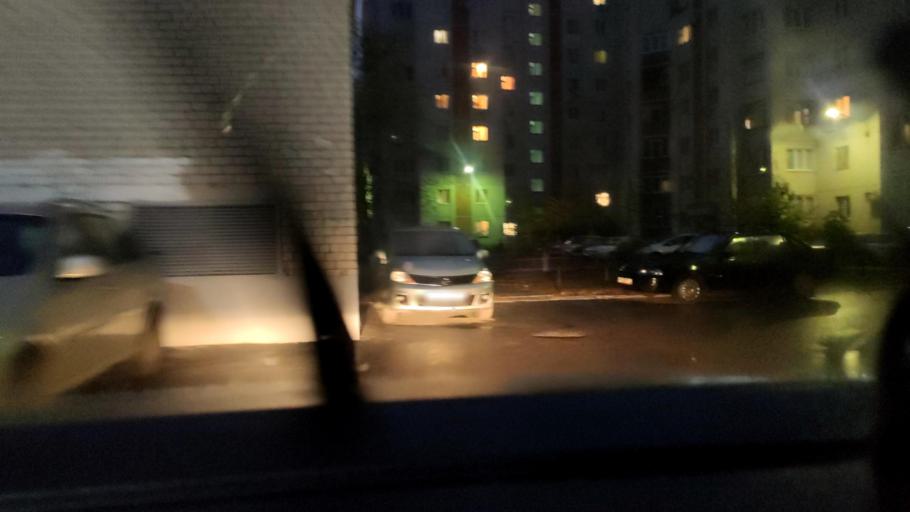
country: RU
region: Voronezj
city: Podgornoye
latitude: 51.7099
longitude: 39.1701
